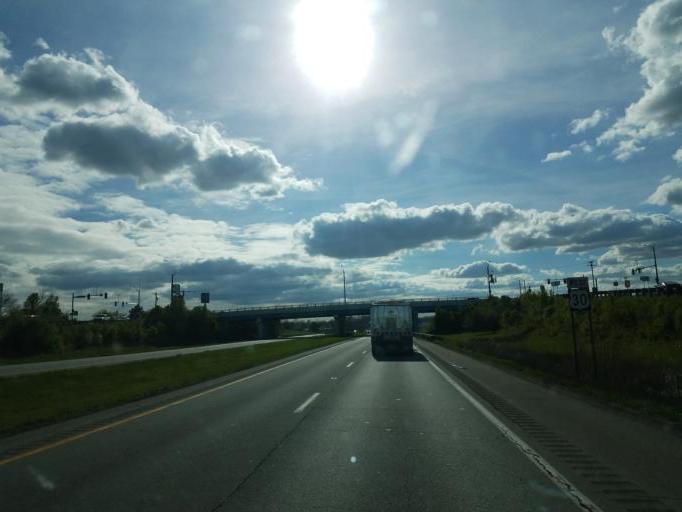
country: US
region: Ohio
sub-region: Richland County
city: Mansfield
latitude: 40.7745
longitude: -82.5503
